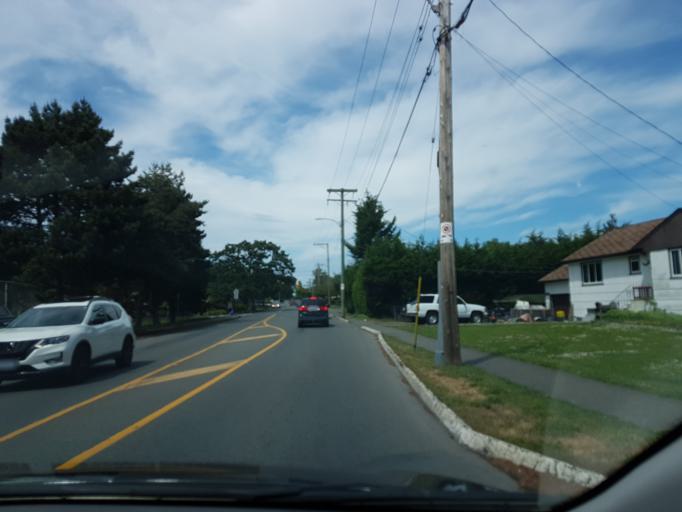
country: CA
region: British Columbia
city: Oak Bay
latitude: 48.4671
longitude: -123.3357
